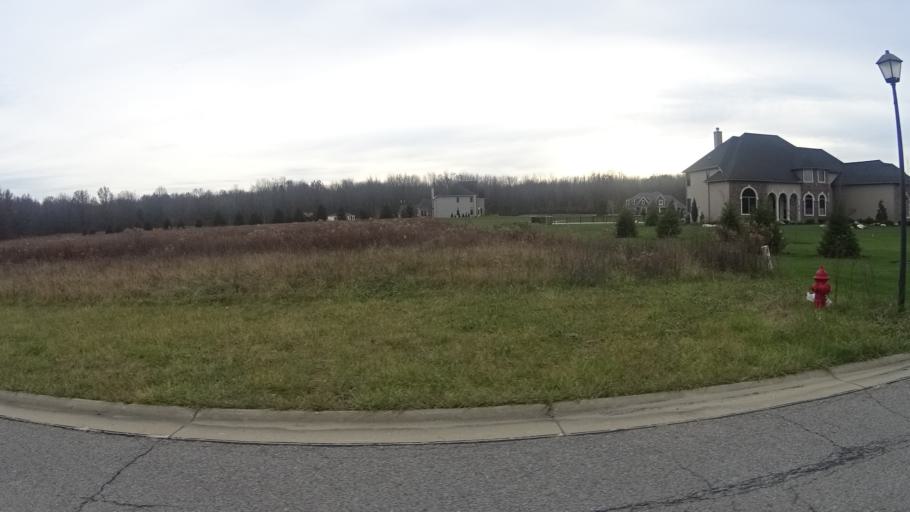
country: US
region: Ohio
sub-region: Cuyahoga County
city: Olmsted Falls
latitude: 41.3460
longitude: -81.9461
